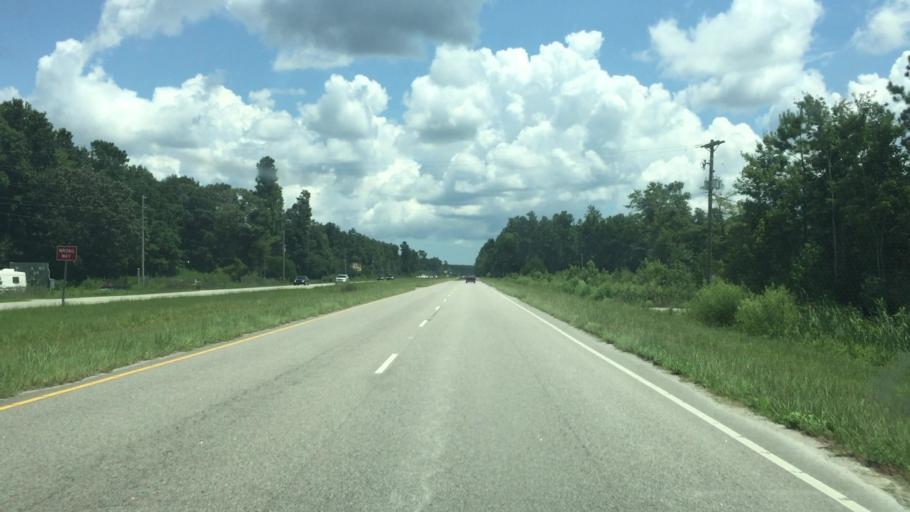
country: US
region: South Carolina
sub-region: Horry County
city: Loris
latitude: 34.0141
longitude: -78.7837
